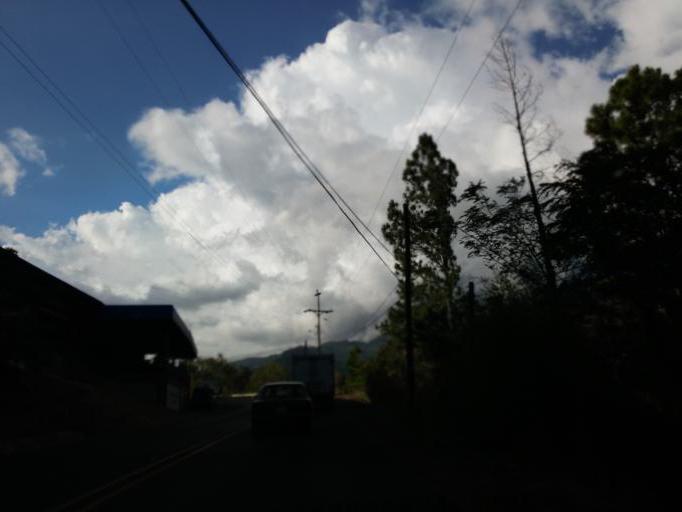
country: CR
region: San Jose
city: San Ignacio
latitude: 9.7975
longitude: -84.1573
